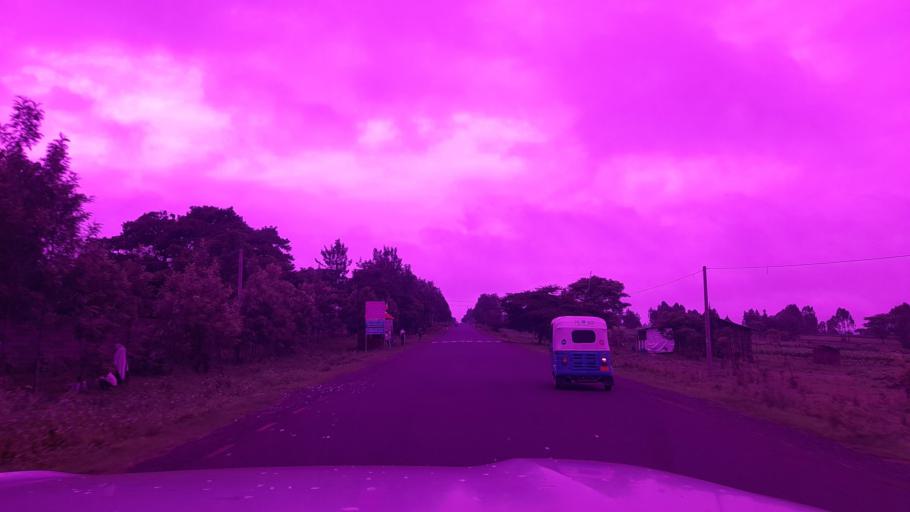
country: ET
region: Oromiya
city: Waliso
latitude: 8.2661
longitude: 37.6556
